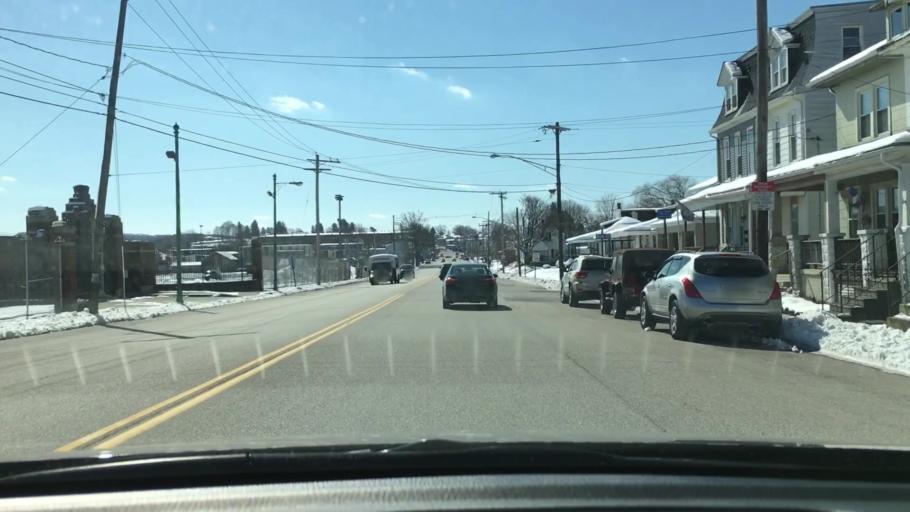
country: US
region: Pennsylvania
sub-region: York County
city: West York
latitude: 39.9589
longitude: -76.7598
